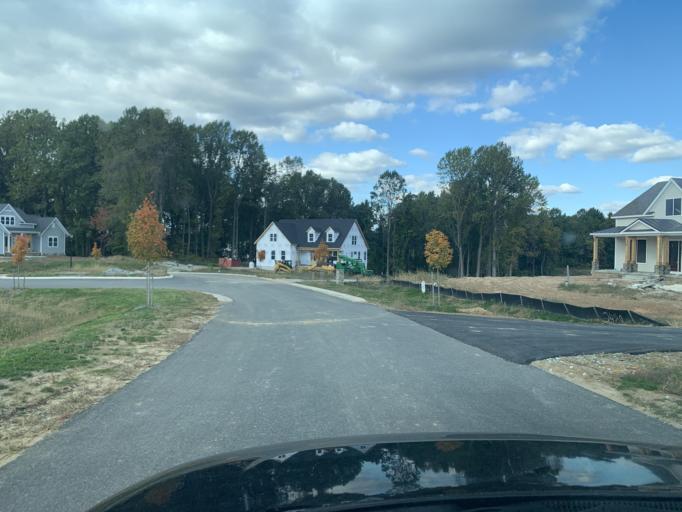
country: US
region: Maryland
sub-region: Harford County
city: Bel Air North
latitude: 39.5863
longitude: -76.4102
